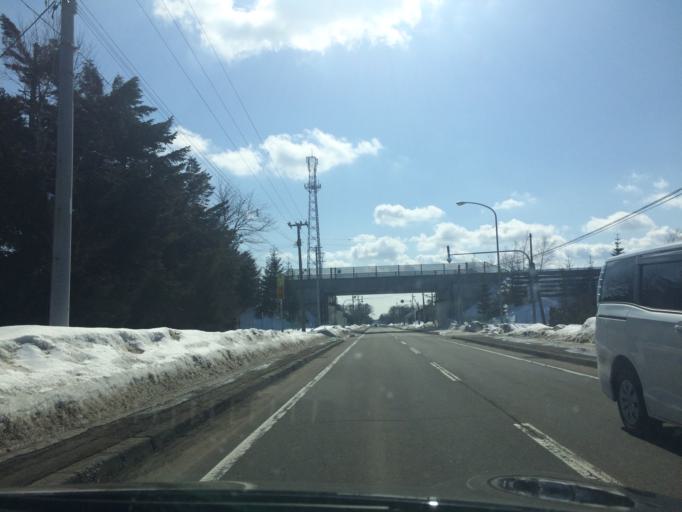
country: JP
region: Hokkaido
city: Chitose
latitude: 42.8838
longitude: 141.6379
